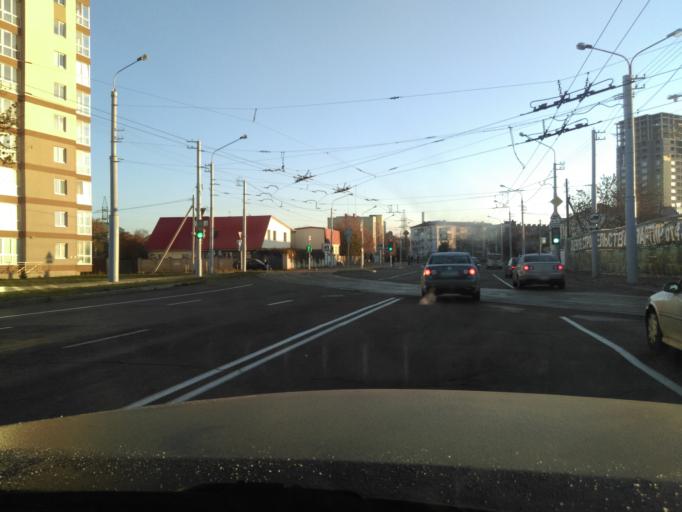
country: BY
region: Minsk
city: Minsk
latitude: 53.8671
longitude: 27.6191
